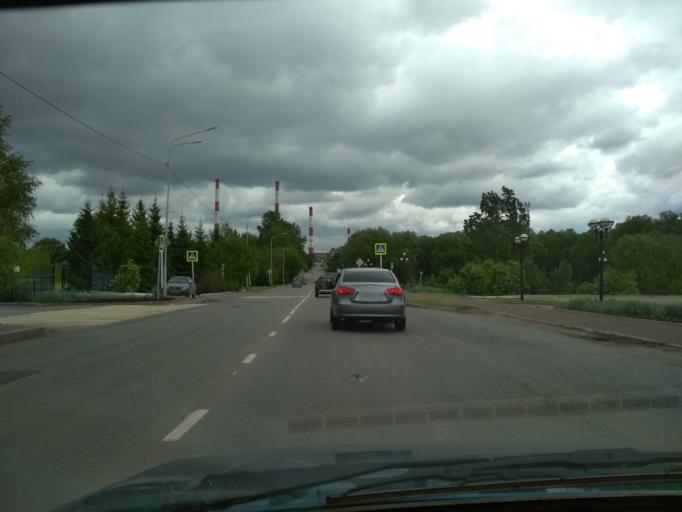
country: RU
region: Tatarstan
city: Zainsk
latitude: 55.2913
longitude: 51.9947
